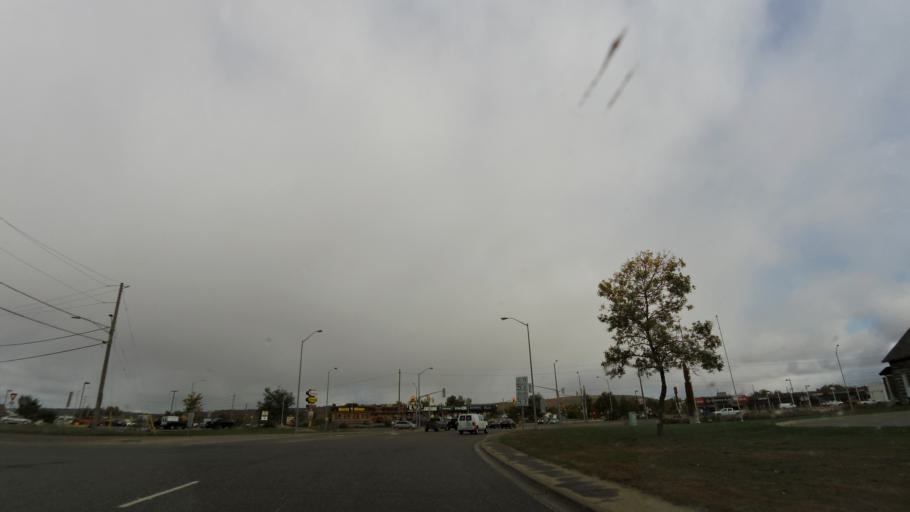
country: CA
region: Ontario
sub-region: Nipissing District
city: North Bay
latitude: 46.3085
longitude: -79.4389
